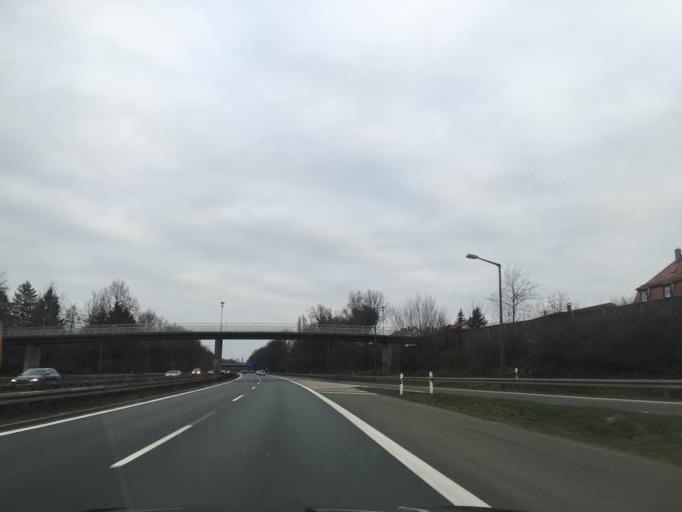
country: DE
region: Bavaria
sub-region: Regierungsbezirk Mittelfranken
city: Furth
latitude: 49.4798
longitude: 11.0065
